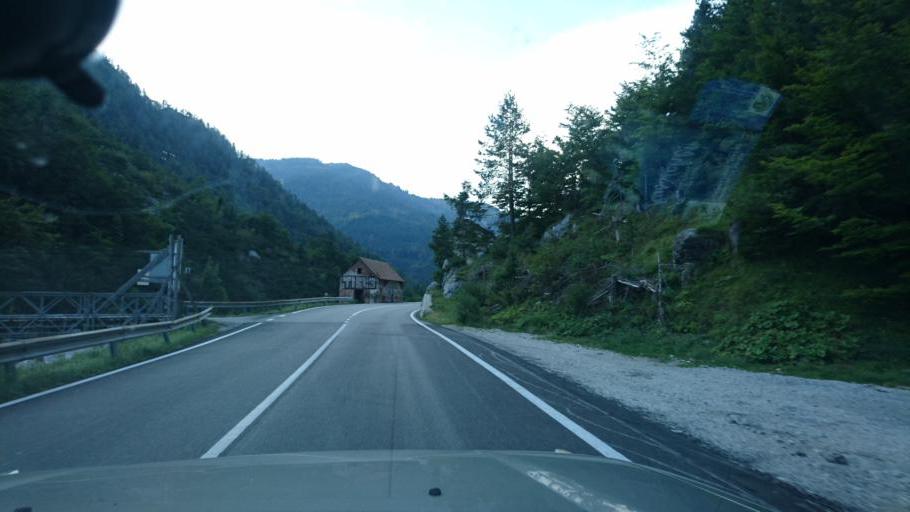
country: IT
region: Friuli Venezia Giulia
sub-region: Provincia di Udine
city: Tarvisio
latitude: 46.4612
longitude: 13.5739
